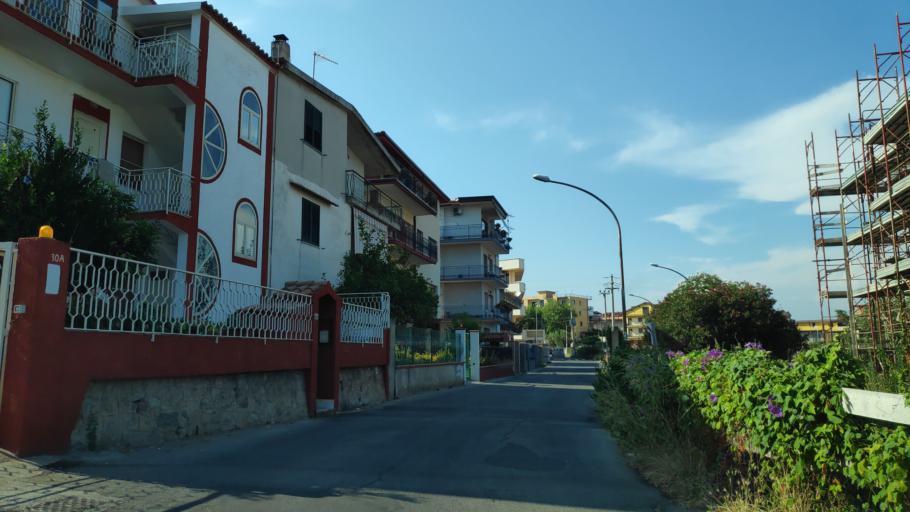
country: IT
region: Calabria
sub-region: Provincia di Catanzaro
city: Soverato Superiore
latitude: 38.6878
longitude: 16.5350
